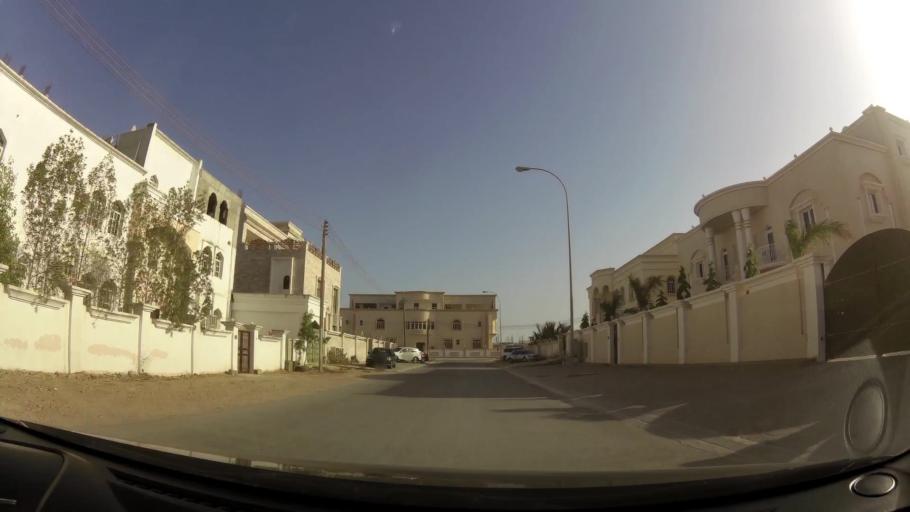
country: OM
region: Zufar
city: Salalah
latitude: 17.0228
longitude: 54.0263
